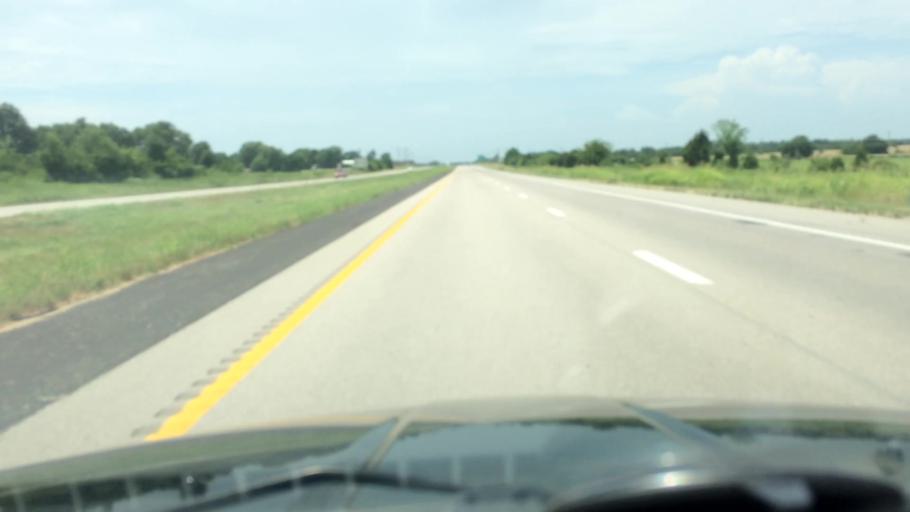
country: US
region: Missouri
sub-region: Polk County
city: Bolivar
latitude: 37.5797
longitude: -93.4051
